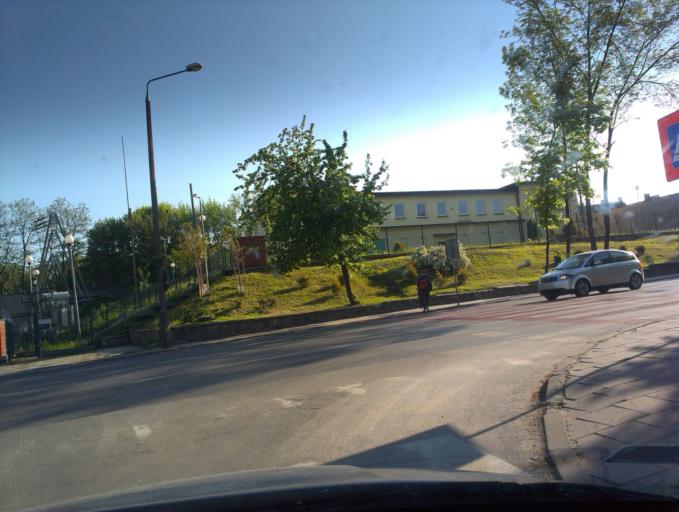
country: PL
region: Masovian Voivodeship
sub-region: Radom
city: Radom
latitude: 51.3972
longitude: 21.1484
